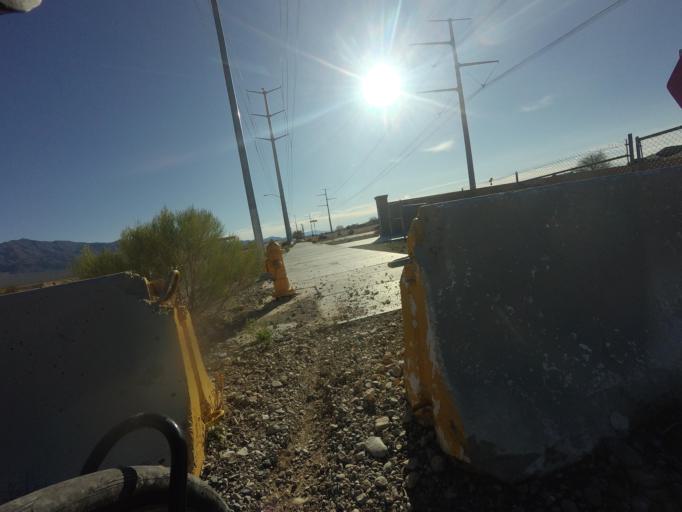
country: US
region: Nevada
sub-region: Clark County
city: North Las Vegas
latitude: 36.3359
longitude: -115.2807
